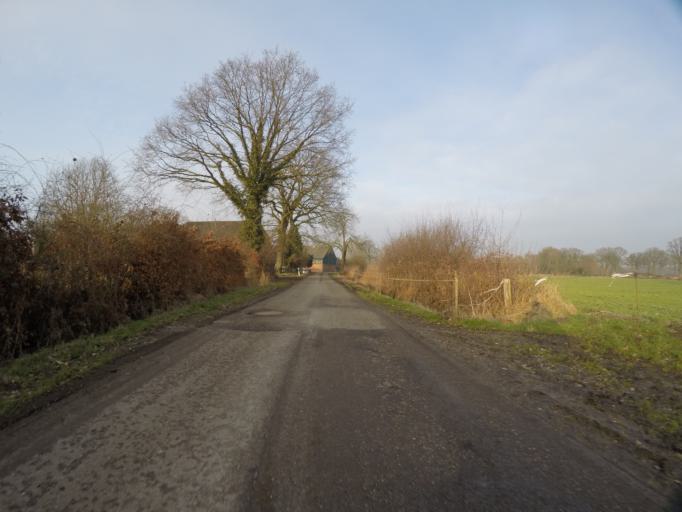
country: DE
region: Schleswig-Holstein
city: Quickborn
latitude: 53.7128
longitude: 9.8936
